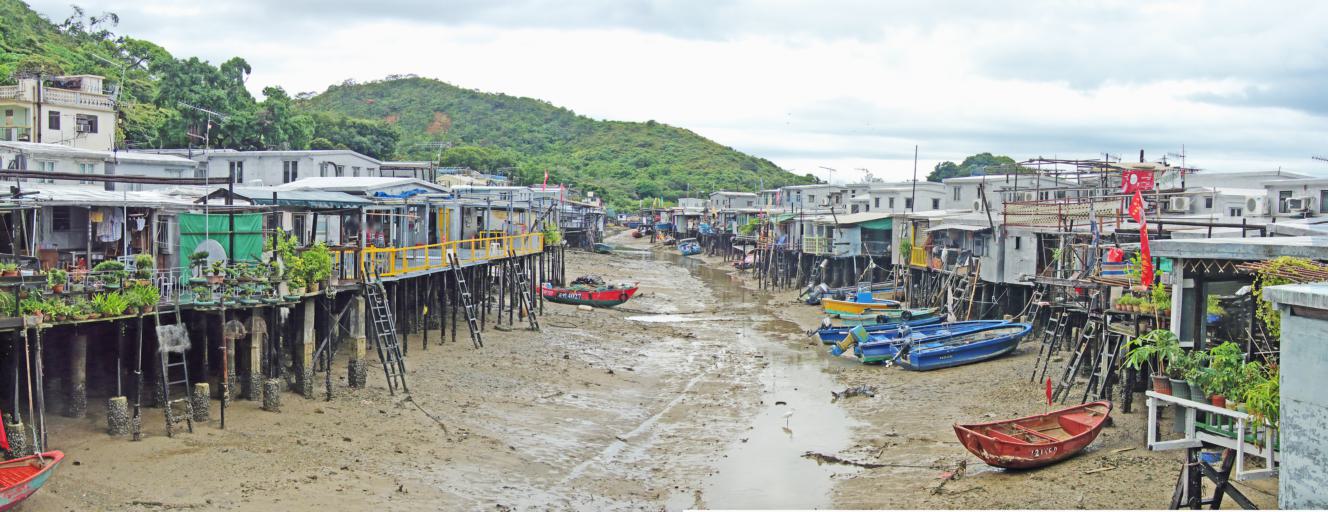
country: HK
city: Tai O
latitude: 22.2539
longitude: 113.8621
